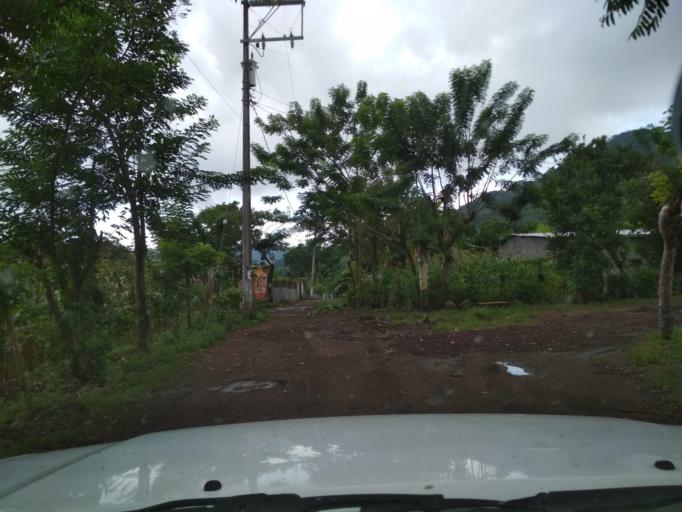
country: MX
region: Veracruz
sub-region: San Andres Tuxtla
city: El Huidero
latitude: 18.3903
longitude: -95.1791
